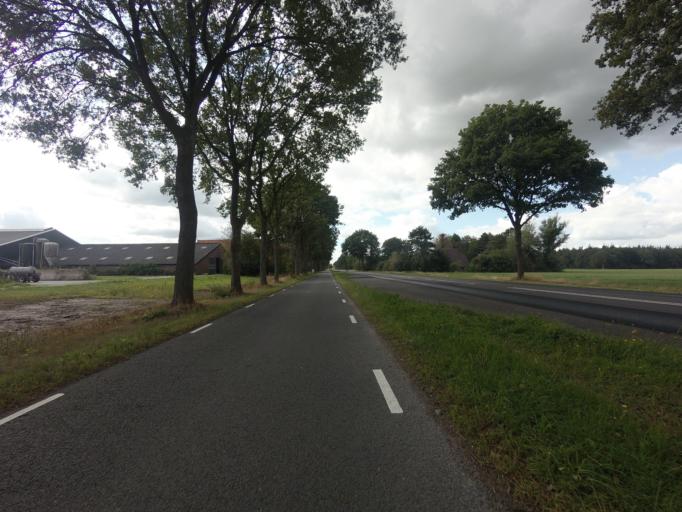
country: NL
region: Friesland
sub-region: Gemeente Heerenveen
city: Jubbega
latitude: 52.9612
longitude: 6.1958
